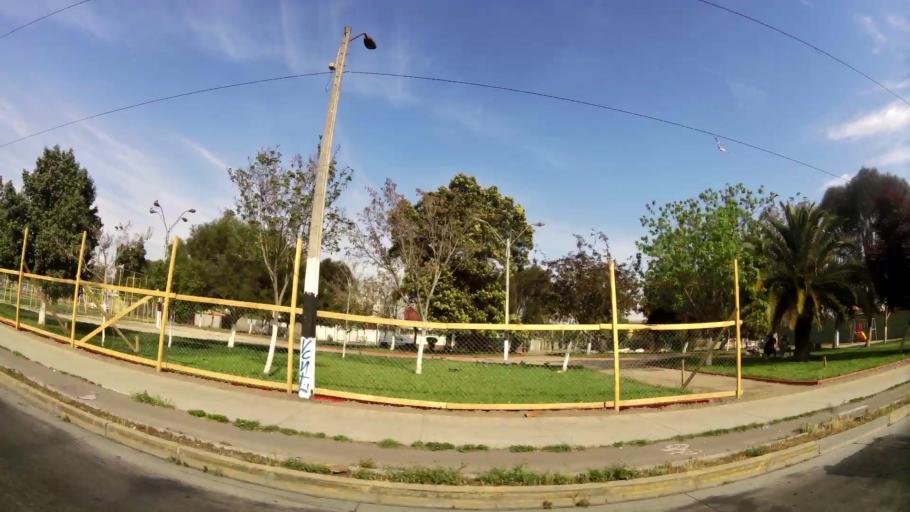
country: CL
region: Santiago Metropolitan
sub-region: Provincia de Santiago
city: La Pintana
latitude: -33.5505
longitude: -70.6329
